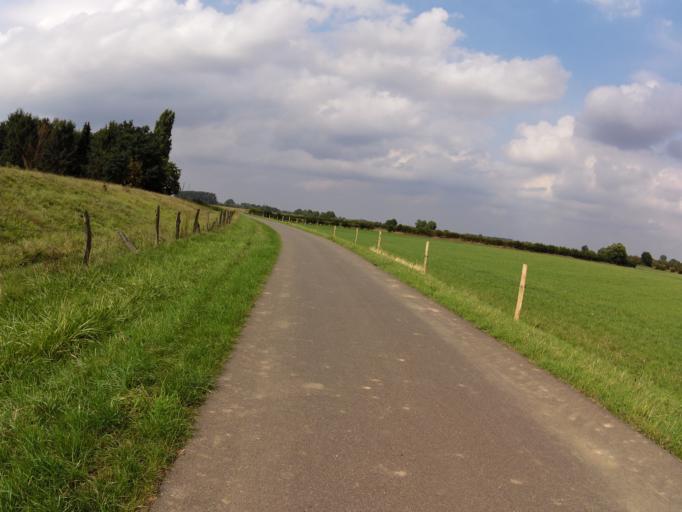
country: DE
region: Lower Saxony
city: Blender
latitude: 52.8941
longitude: 9.1682
